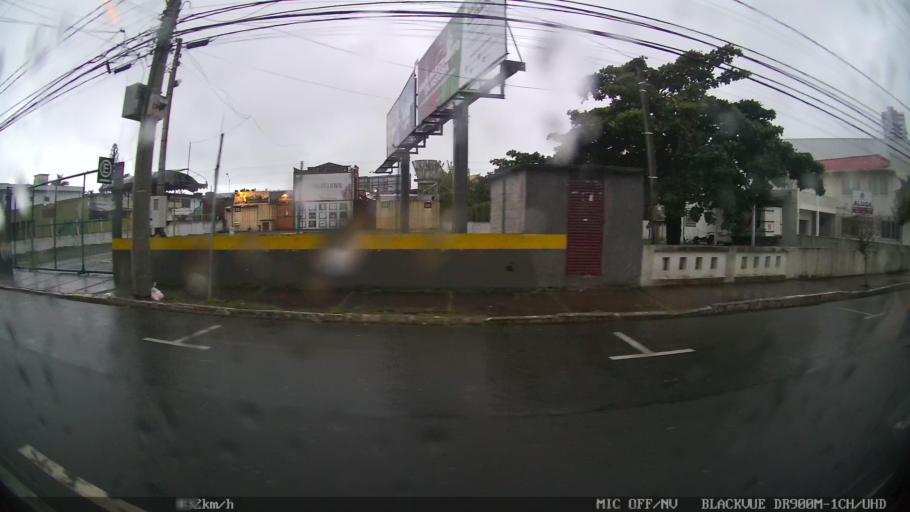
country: BR
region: Santa Catarina
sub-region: Itajai
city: Itajai
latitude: -26.9166
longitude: -48.6535
